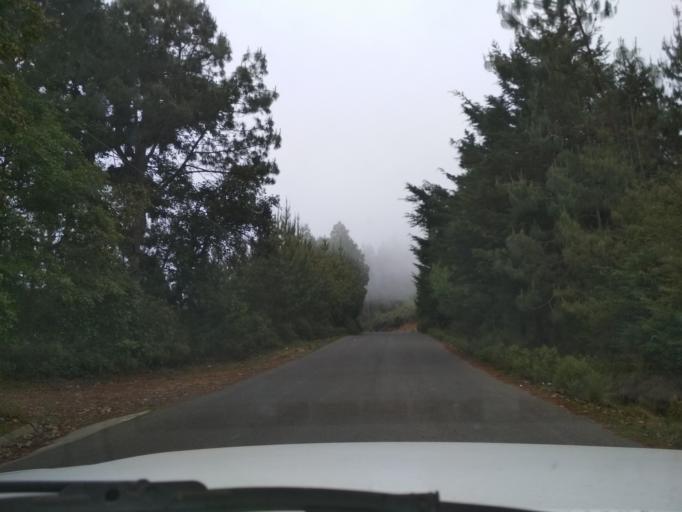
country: MX
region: Veracruz
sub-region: Mariano Escobedo
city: Loma Grande
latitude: 18.9303
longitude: -97.2209
